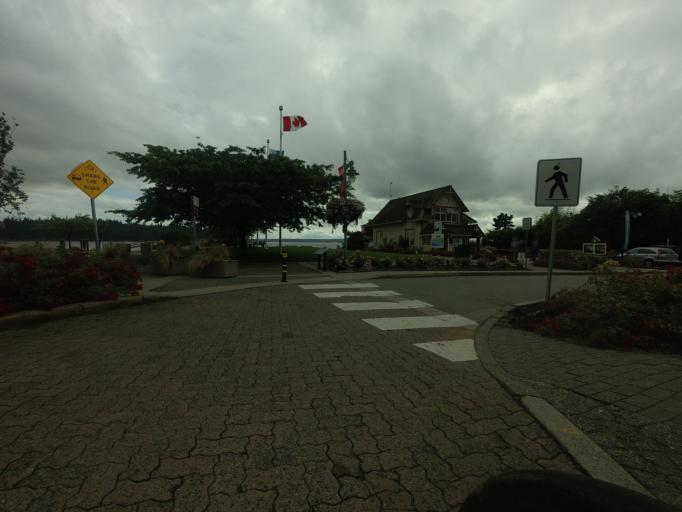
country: CA
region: British Columbia
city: West Vancouver
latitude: 49.3272
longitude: -123.1546
